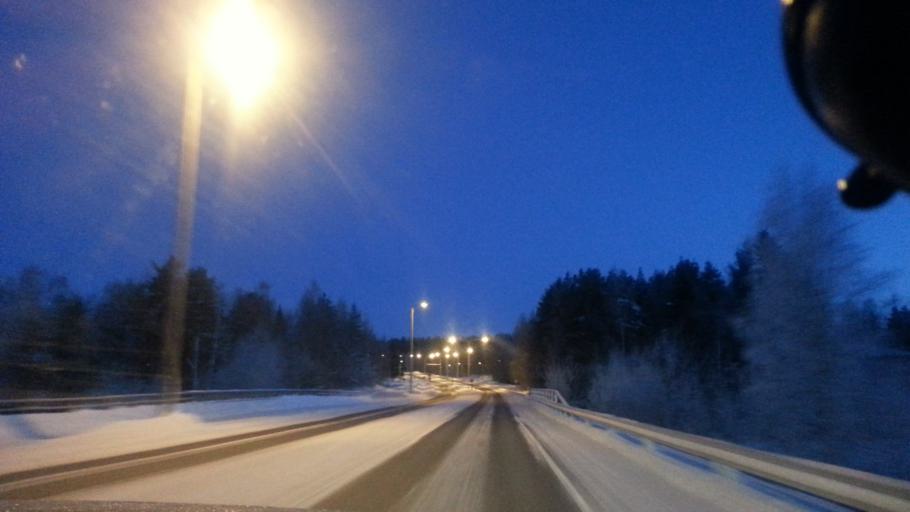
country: FI
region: Lapland
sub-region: Rovaniemi
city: Rovaniemi
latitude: 66.4883
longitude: 25.7536
